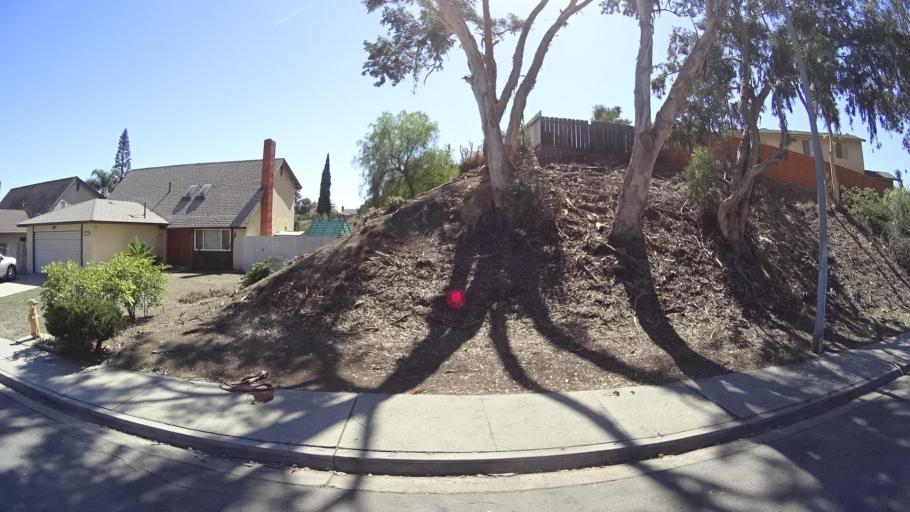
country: US
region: California
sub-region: San Diego County
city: La Presa
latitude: 32.6955
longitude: -117.0200
